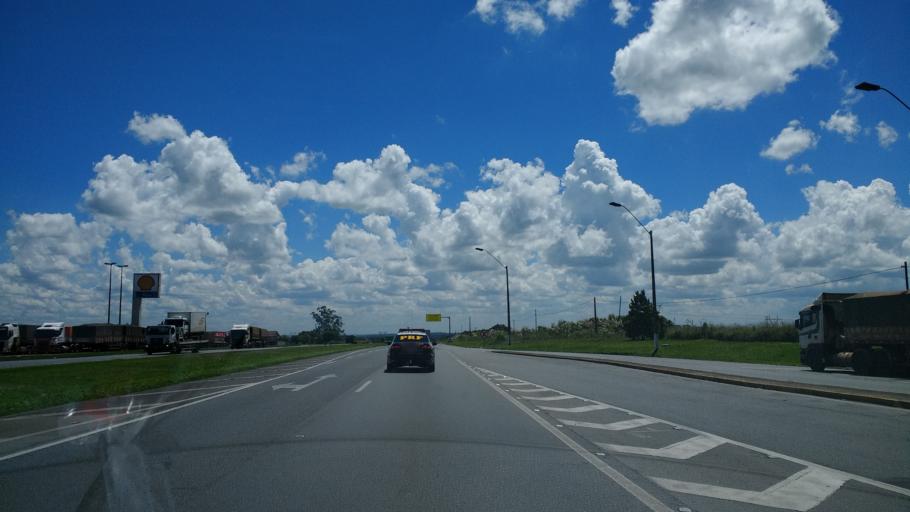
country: BR
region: Parana
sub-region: Campo Largo
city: Campo Largo
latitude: -25.4716
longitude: -49.6672
